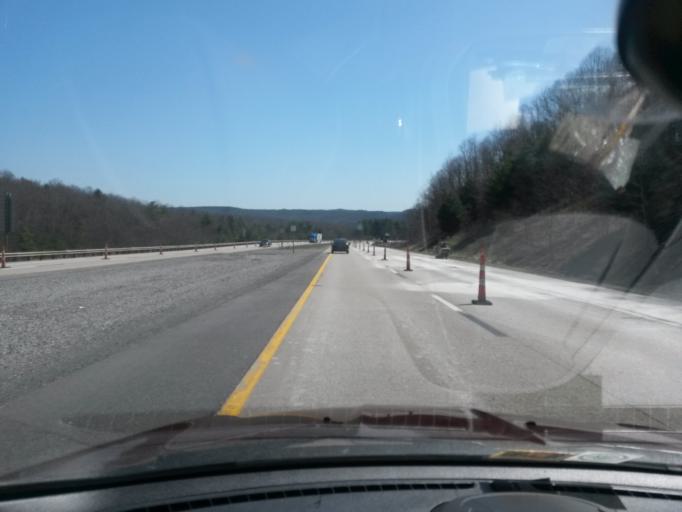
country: US
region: West Virginia
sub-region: Raleigh County
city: Daniels
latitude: 37.7730
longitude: -81.0543
